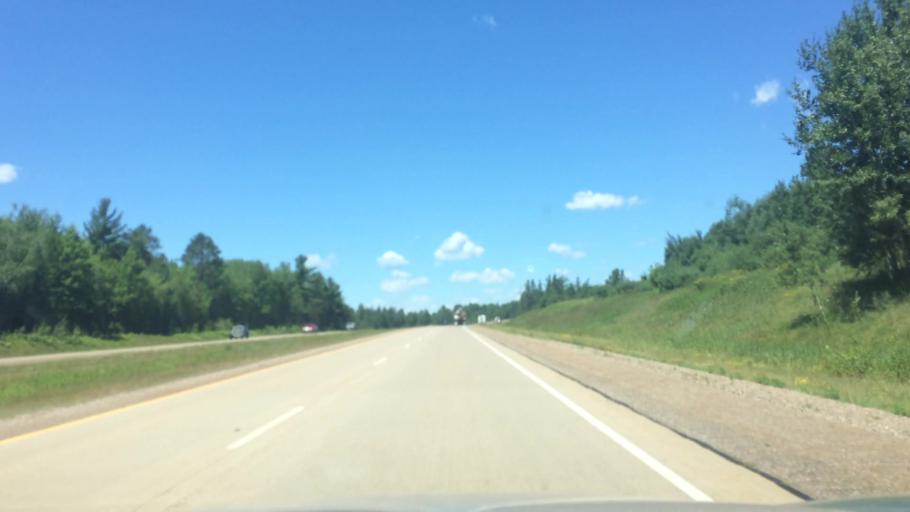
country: US
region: Wisconsin
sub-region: Lincoln County
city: Tomahawk
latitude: 45.4406
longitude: -89.6833
